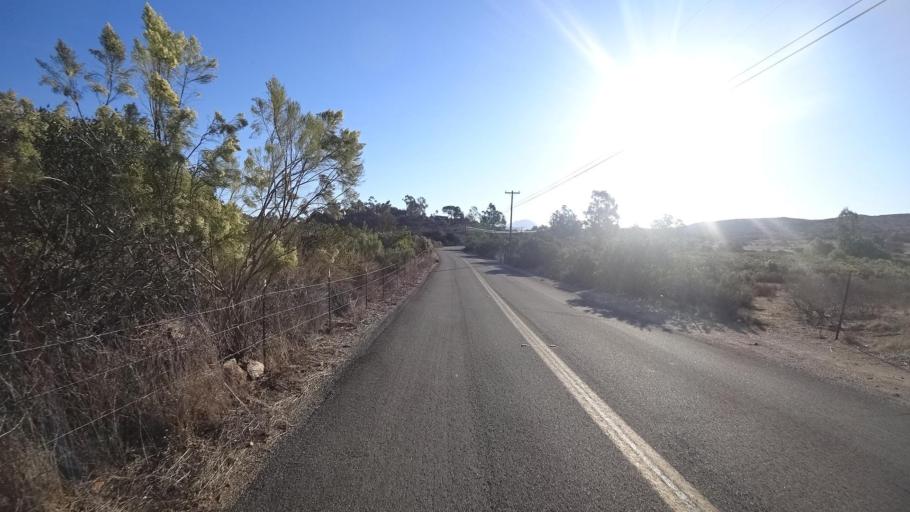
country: US
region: California
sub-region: San Diego County
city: Jamul
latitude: 32.7040
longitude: -116.8959
